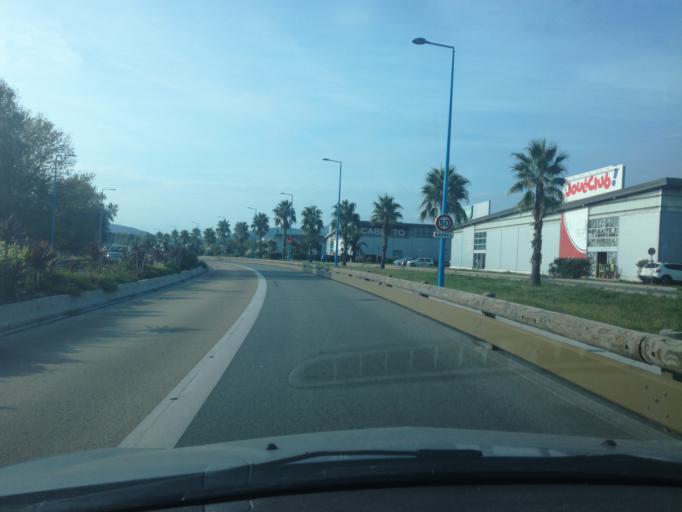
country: FR
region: Provence-Alpes-Cote d'Azur
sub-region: Departement des Alpes-Maritimes
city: Mandelieu-la-Napoule
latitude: 43.5555
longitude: 6.9471
